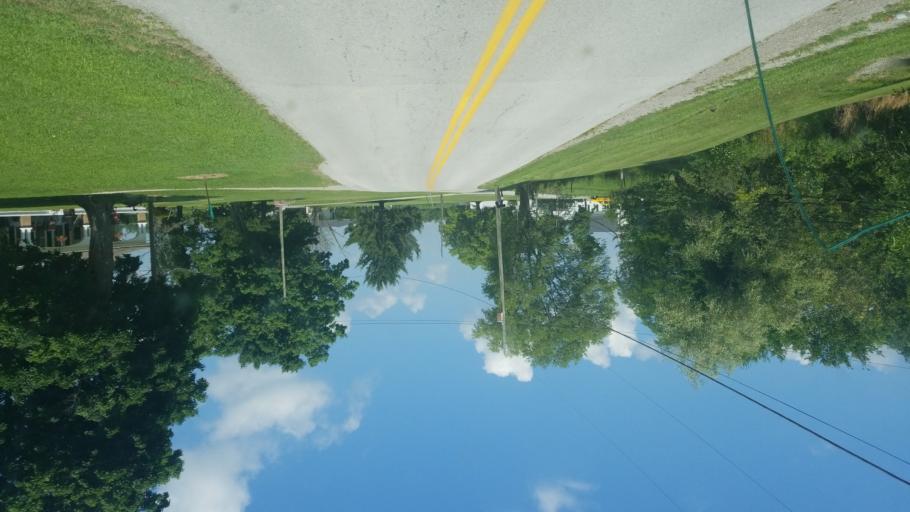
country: US
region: Ohio
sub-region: Allen County
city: Lima
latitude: 40.6938
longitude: -83.9739
